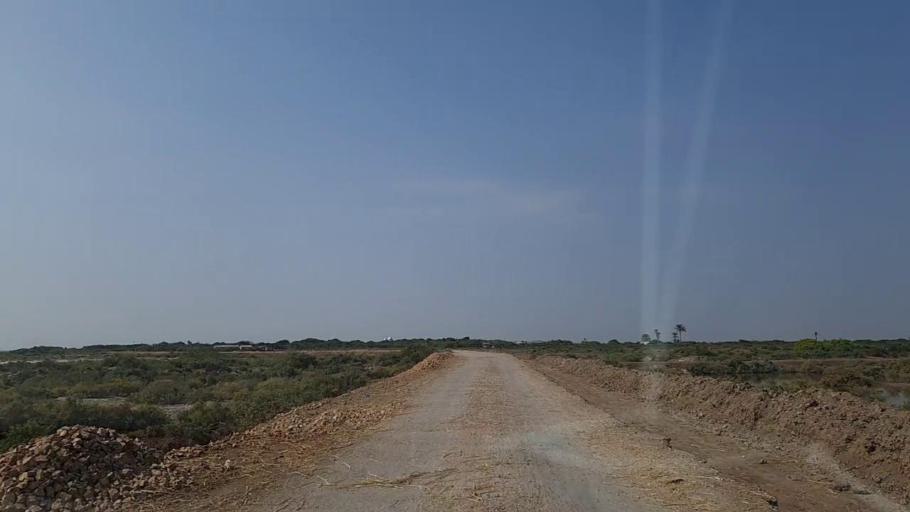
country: PK
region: Sindh
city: Chuhar Jamali
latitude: 24.1999
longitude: 67.8251
